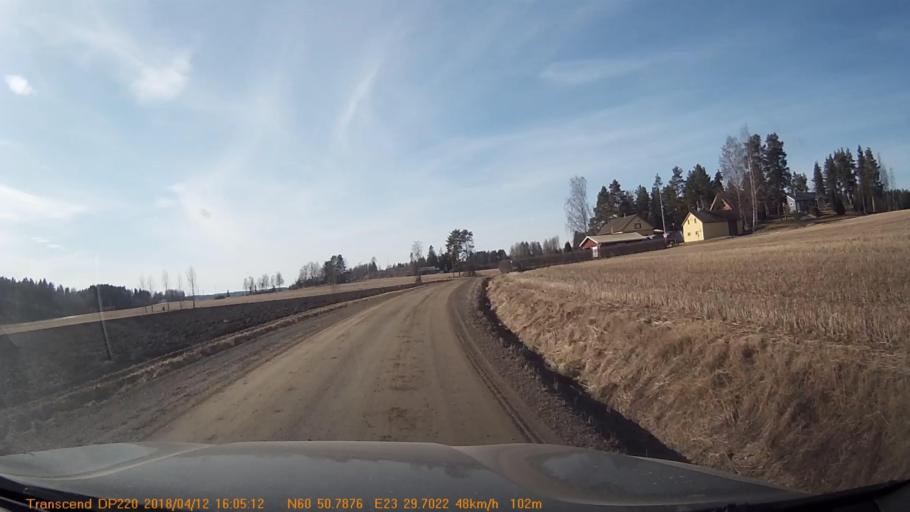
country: FI
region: Haeme
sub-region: Forssa
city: Jokioinen
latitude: 60.8465
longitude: 23.4948
